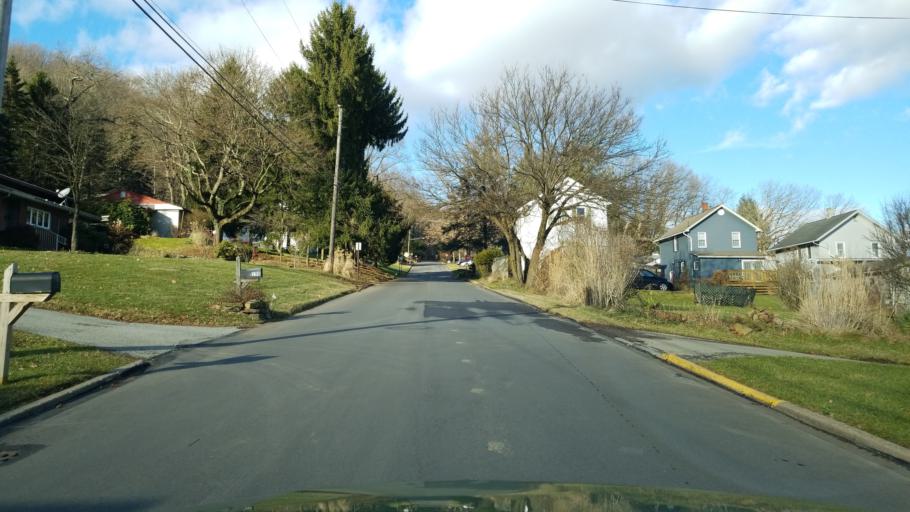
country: US
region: Pennsylvania
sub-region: Indiana County
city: Indiana
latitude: 40.6250
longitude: -79.1634
